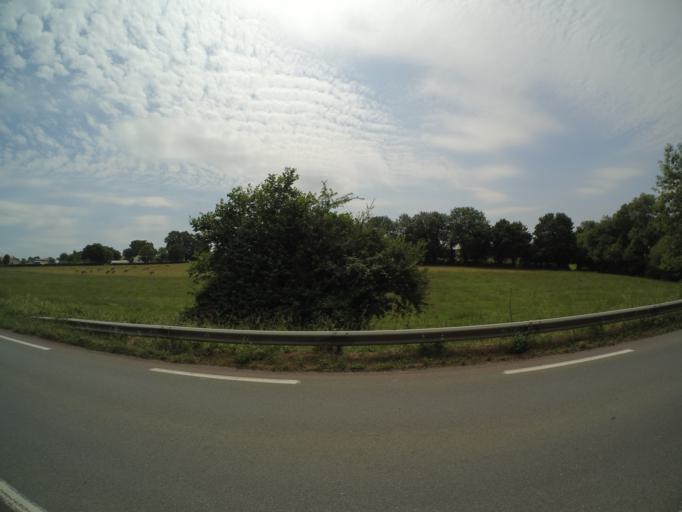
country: FR
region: Pays de la Loire
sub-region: Departement de la Vendee
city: Vendrennes
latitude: 46.8425
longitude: -1.0797
